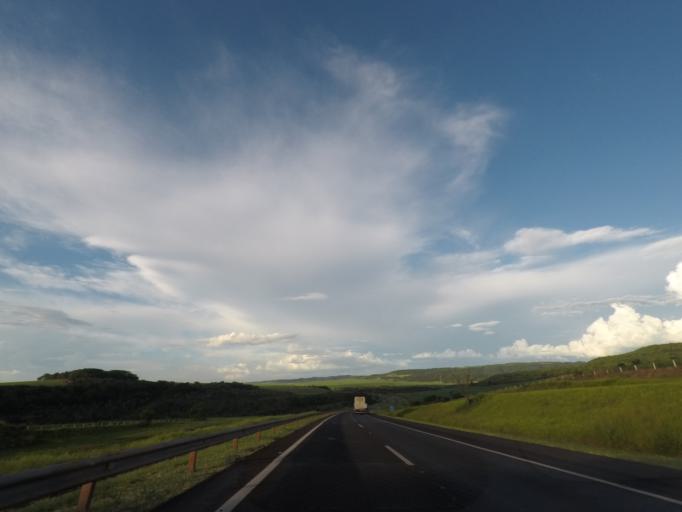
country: BR
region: Sao Paulo
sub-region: Ituverava
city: Ituverava
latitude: -20.2442
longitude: -47.7975
